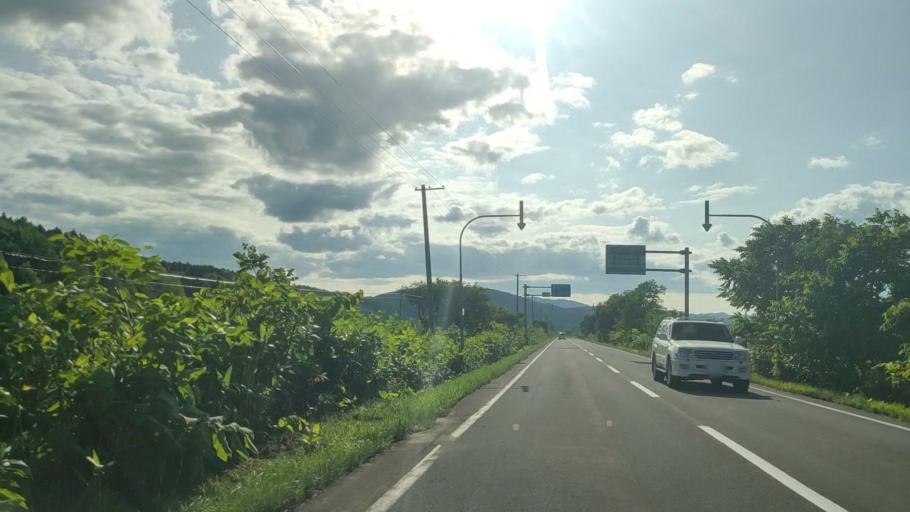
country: JP
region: Hokkaido
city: Nayoro
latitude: 44.7308
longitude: 142.0903
